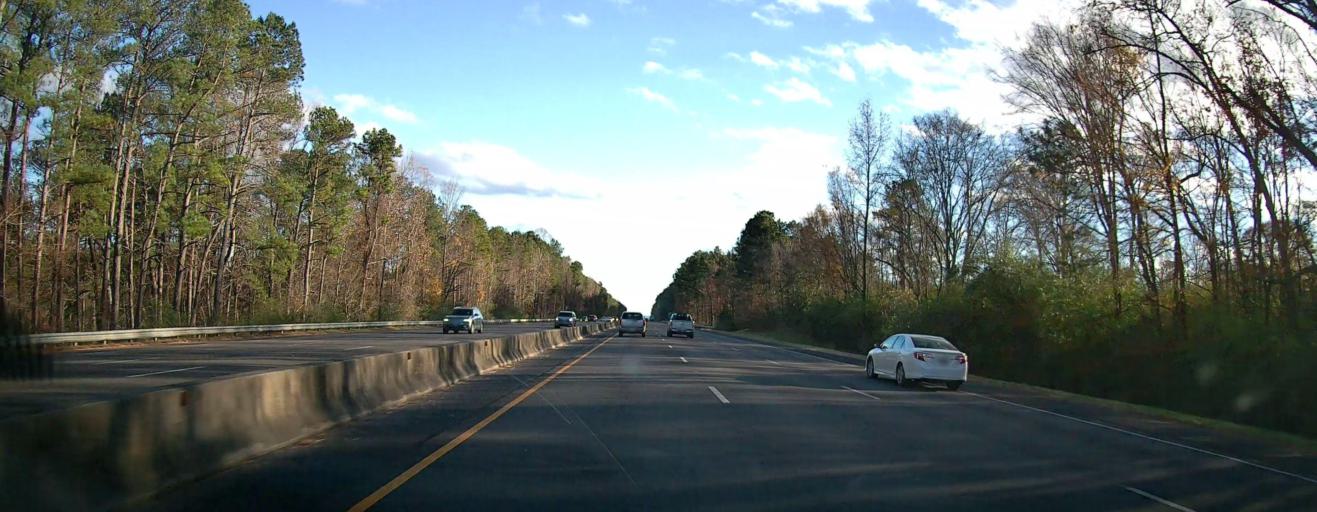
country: US
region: Alabama
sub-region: Blount County
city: Smoke Rise
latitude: 33.8672
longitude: -86.8340
